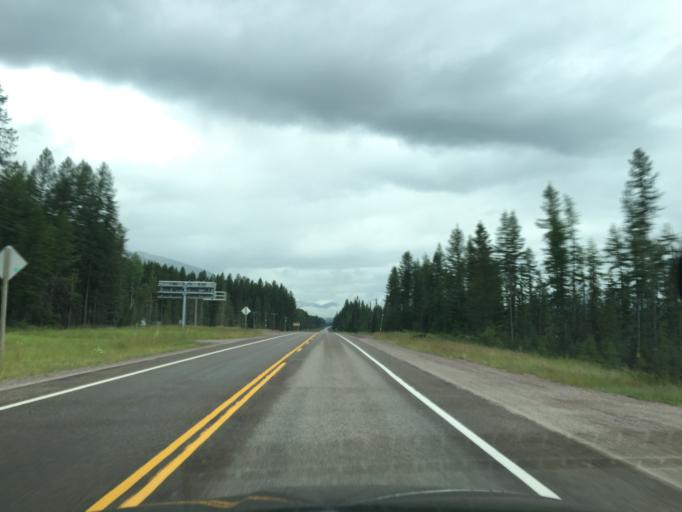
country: US
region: Montana
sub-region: Flathead County
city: Bigfork
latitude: 48.2847
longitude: -113.6071
